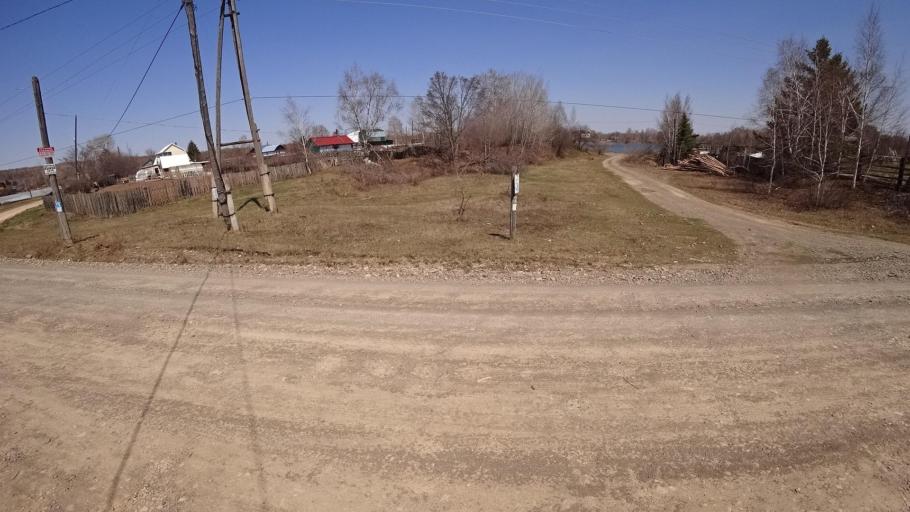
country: RU
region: Khabarovsk Krai
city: Khurba
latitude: 50.4080
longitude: 136.8685
